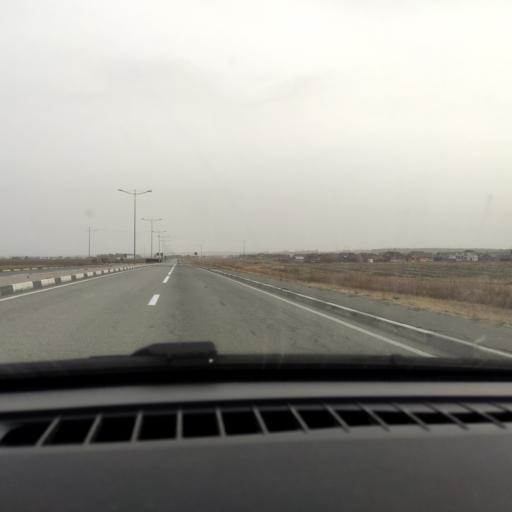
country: RU
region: Belgorod
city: Razumnoye
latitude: 50.5686
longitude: 36.7464
